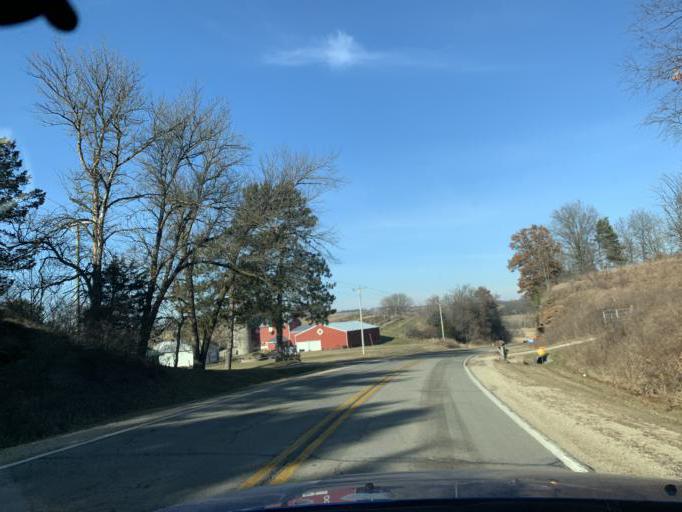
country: US
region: Wisconsin
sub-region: Green County
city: New Glarus
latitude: 42.7831
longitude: -89.8613
